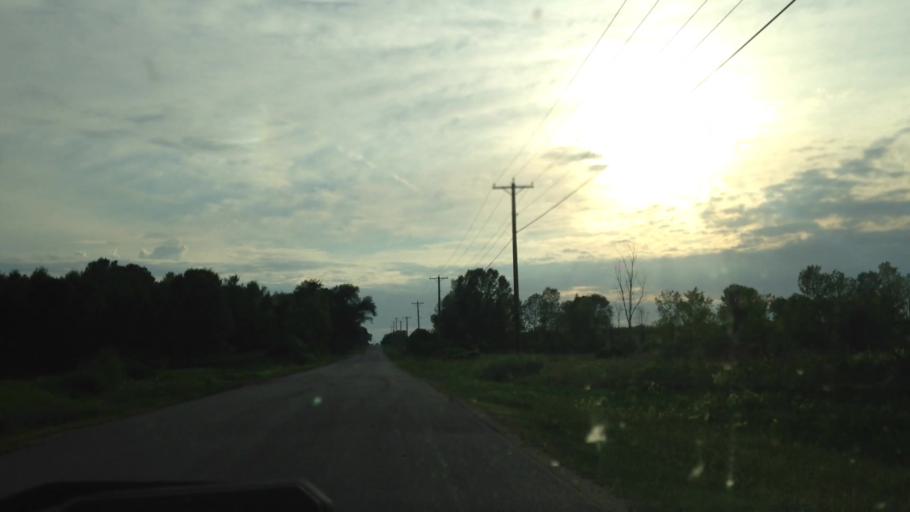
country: US
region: Wisconsin
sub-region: Dodge County
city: Mayville
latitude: 43.4932
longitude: -88.5001
